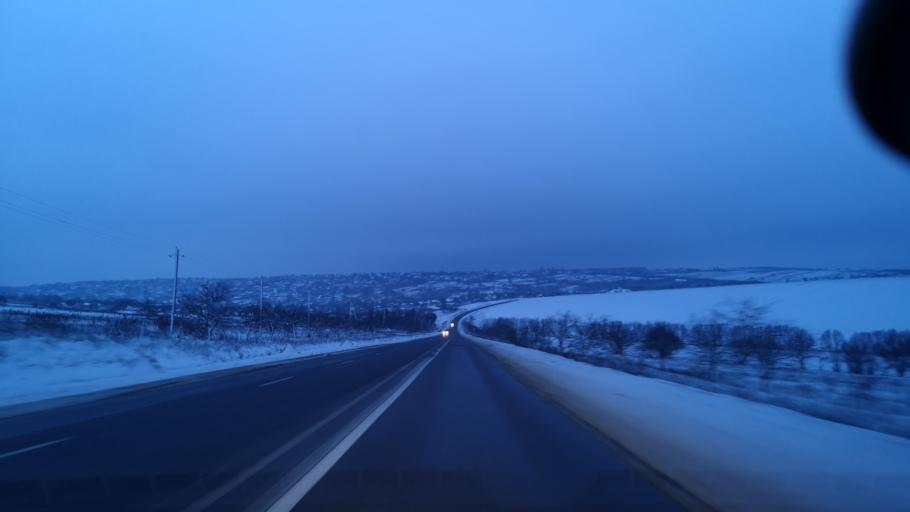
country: MD
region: Soldanesti
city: Soldanesti
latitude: 47.7123
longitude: 28.8474
